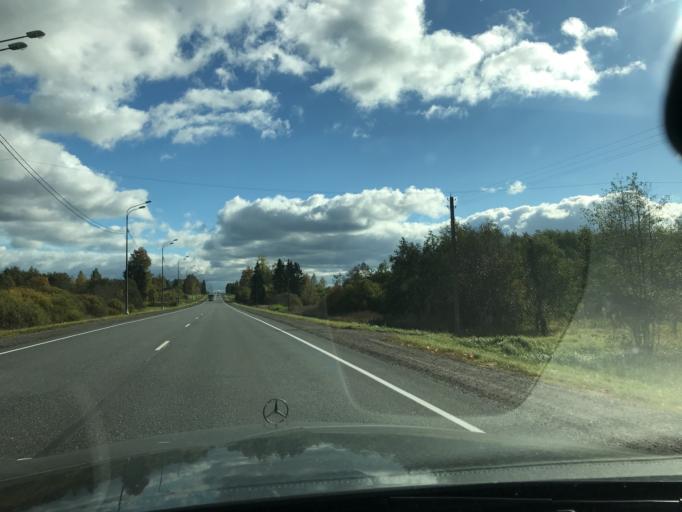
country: RU
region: Pskov
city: Ostrov
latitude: 57.1237
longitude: 28.5249
